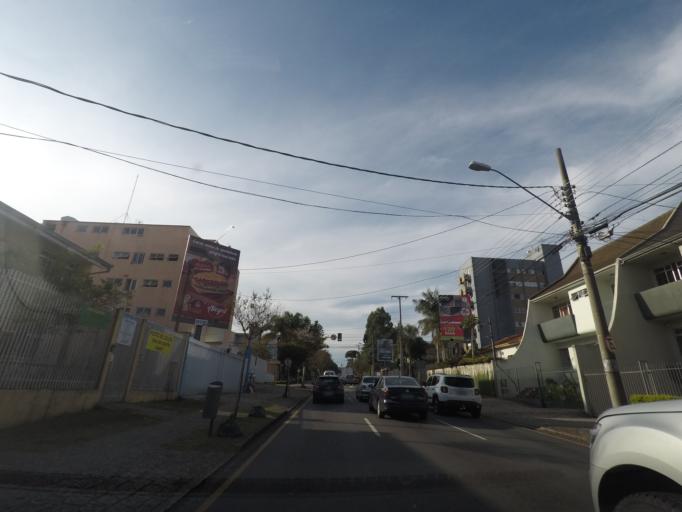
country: BR
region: Parana
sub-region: Curitiba
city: Curitiba
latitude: -25.4187
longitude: -49.2527
